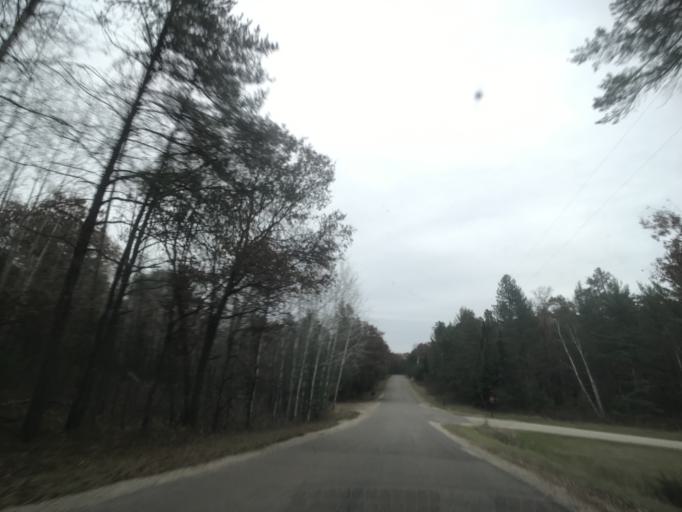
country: US
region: Wisconsin
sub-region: Oconto County
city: Gillett
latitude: 45.2709
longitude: -88.2567
